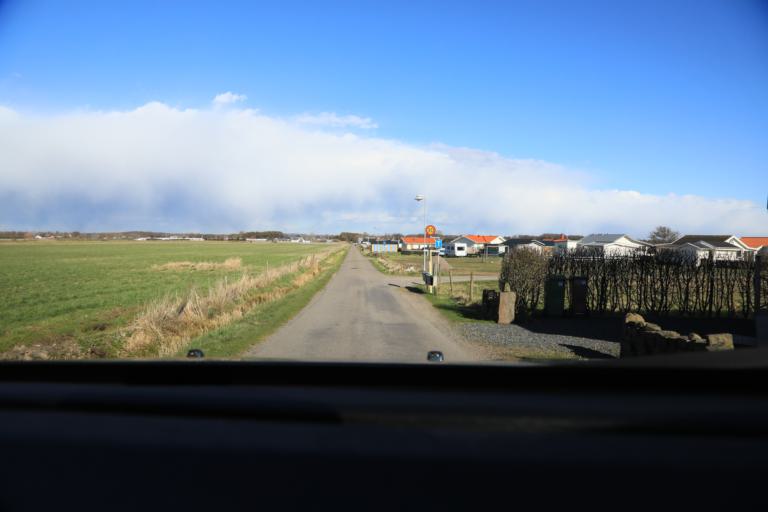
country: SE
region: Halland
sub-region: Varbergs Kommun
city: Traslovslage
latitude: 57.0711
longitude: 12.2680
